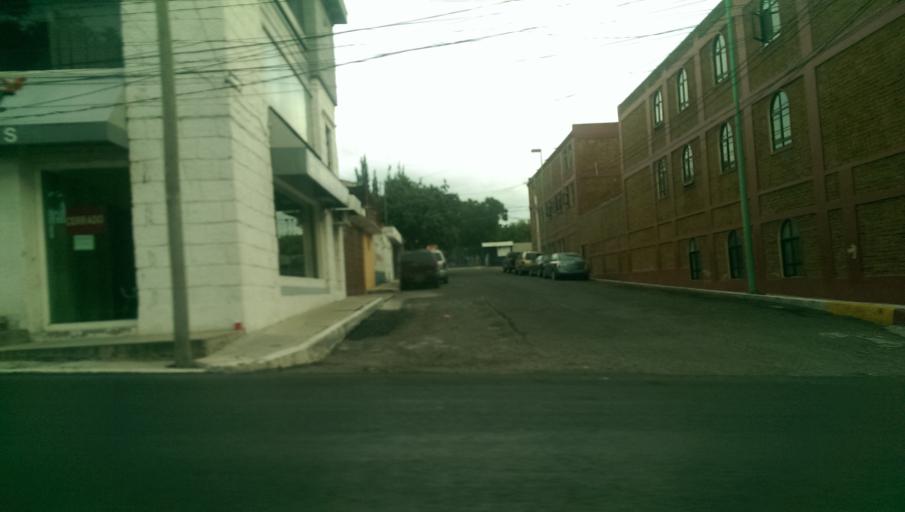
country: MX
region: Queretaro
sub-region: Queretaro
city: Santiago de Queretaro
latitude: 20.5979
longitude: -100.3706
